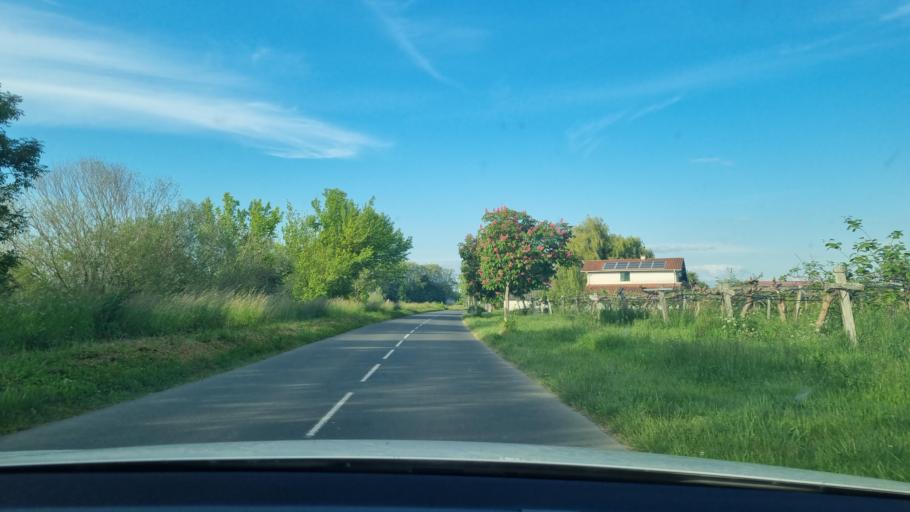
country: FR
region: Aquitaine
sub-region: Departement des Pyrenees-Atlantiques
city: Bardos
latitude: 43.5432
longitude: -1.1979
